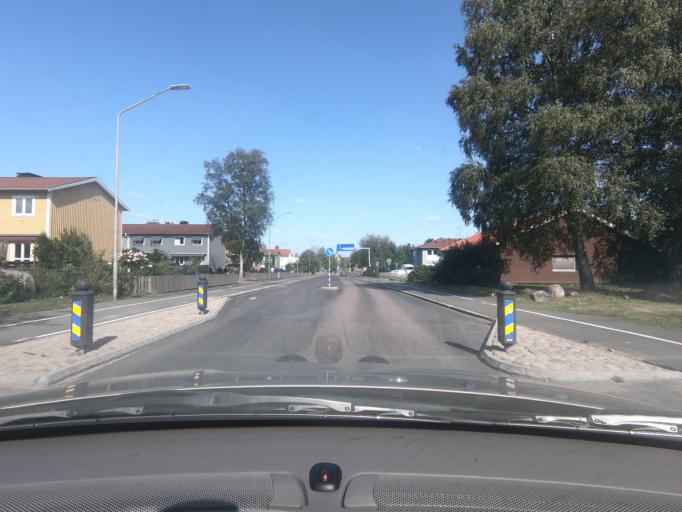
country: SE
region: Joenkoeping
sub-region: Vetlanda Kommun
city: Vetlanda
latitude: 57.4291
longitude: 15.0658
